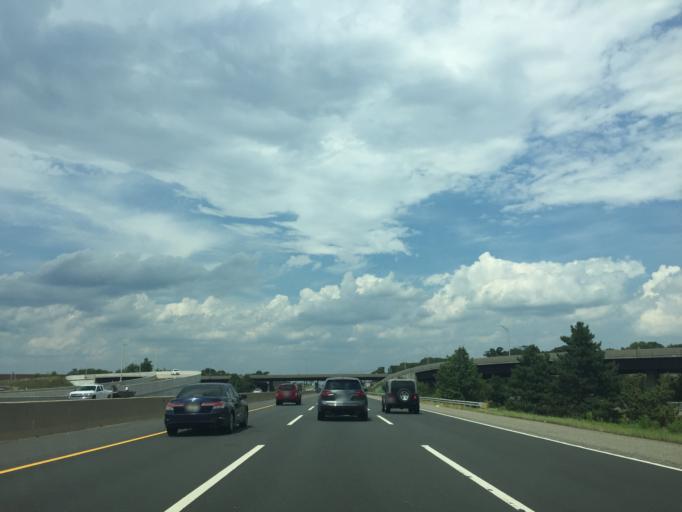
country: US
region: New Jersey
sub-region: Middlesex County
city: Rossmoor
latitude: 40.3487
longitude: -74.4742
